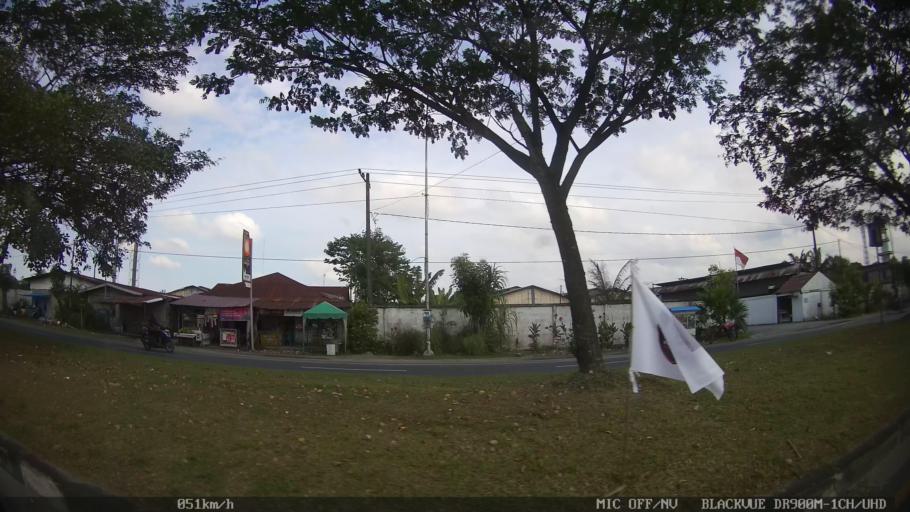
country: ID
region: North Sumatra
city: Percut
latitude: 3.5657
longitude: 98.7942
